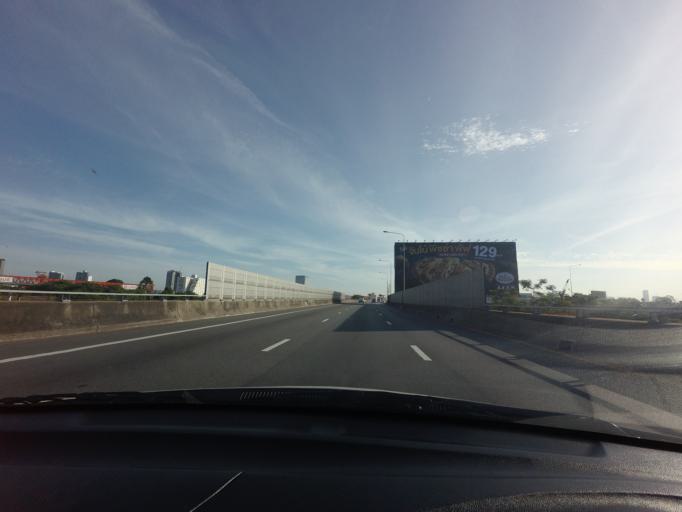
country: TH
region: Bangkok
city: Bang Sue
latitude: 13.7959
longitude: 100.5390
